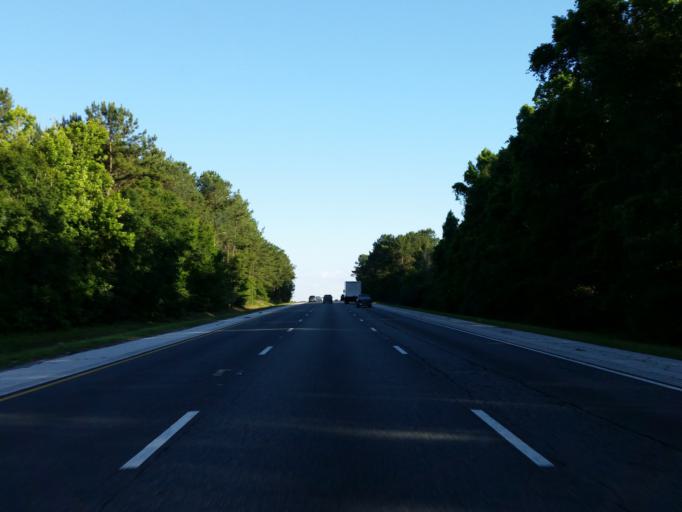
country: US
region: Florida
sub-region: Marion County
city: Citra
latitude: 29.3538
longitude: -82.2212
